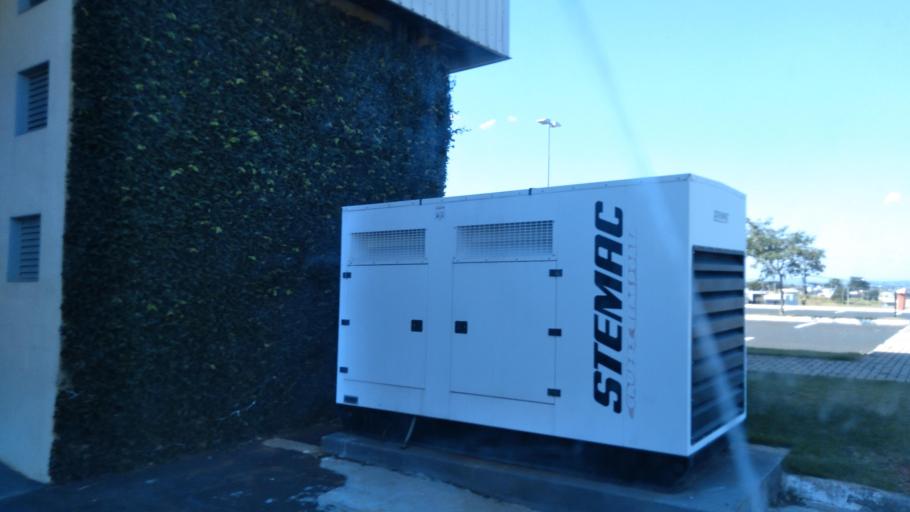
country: BR
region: Goias
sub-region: Mineiros
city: Mineiros
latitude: -17.5503
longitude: -52.5441
